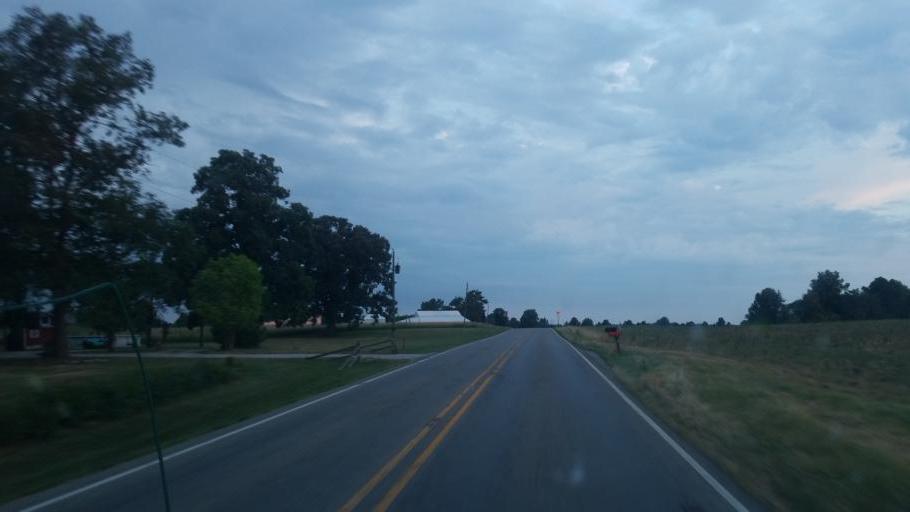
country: US
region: Ohio
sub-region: Defiance County
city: Hicksville
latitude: 41.3330
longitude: -84.8144
